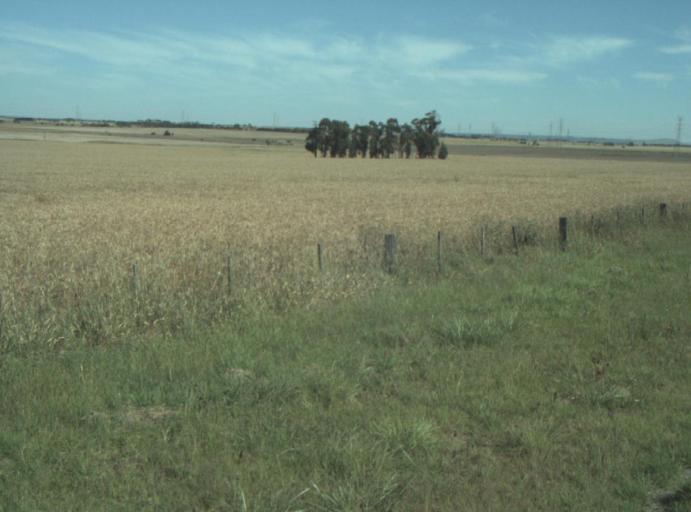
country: AU
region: Victoria
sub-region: Greater Geelong
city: Bell Post Hill
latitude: -38.0740
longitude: 144.3089
